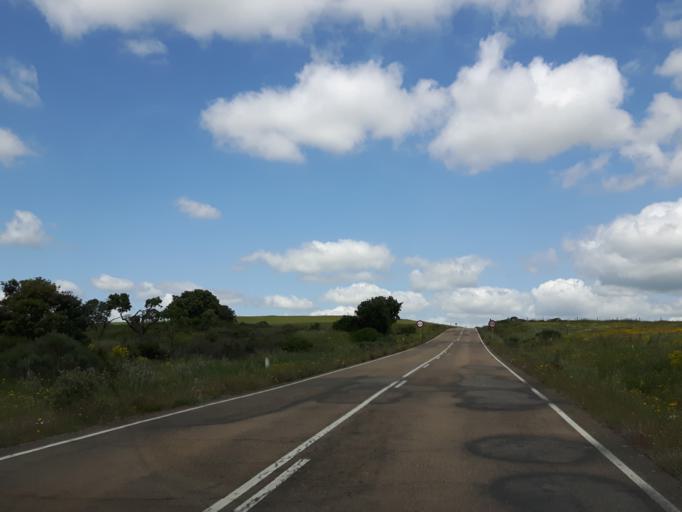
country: ES
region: Castille and Leon
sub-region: Provincia de Salamanca
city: Villar de la Yegua
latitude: 40.7164
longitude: -6.6932
